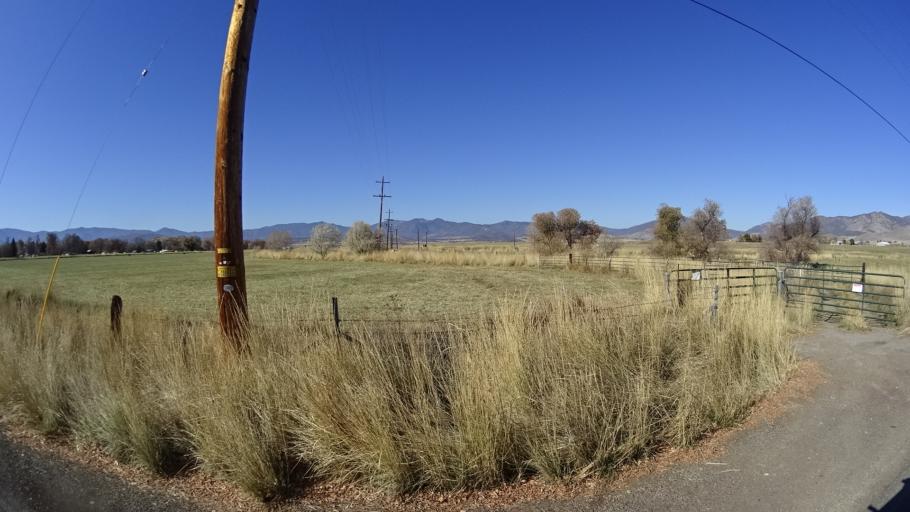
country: US
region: California
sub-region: Siskiyou County
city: Montague
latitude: 41.7347
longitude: -122.5245
